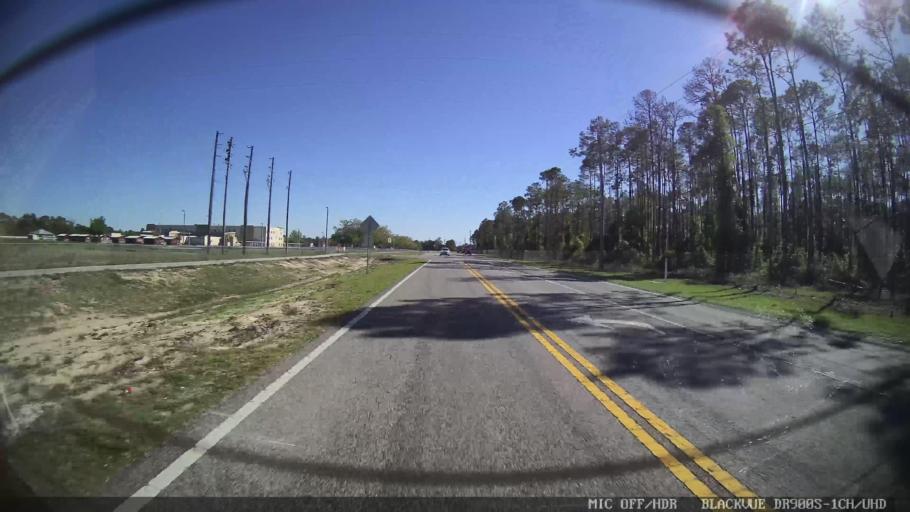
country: US
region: Florida
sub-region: Pasco County
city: Shady Hills
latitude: 28.3790
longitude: -82.5511
